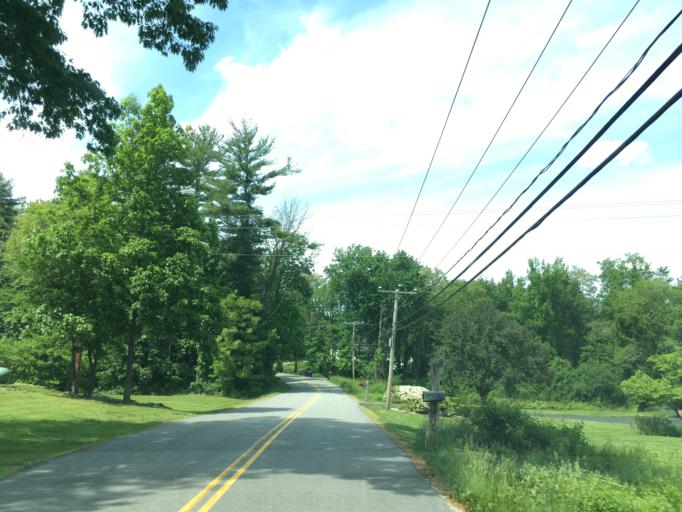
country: US
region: New Hampshire
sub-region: Rockingham County
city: Stratham Station
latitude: 43.0281
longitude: -70.8703
